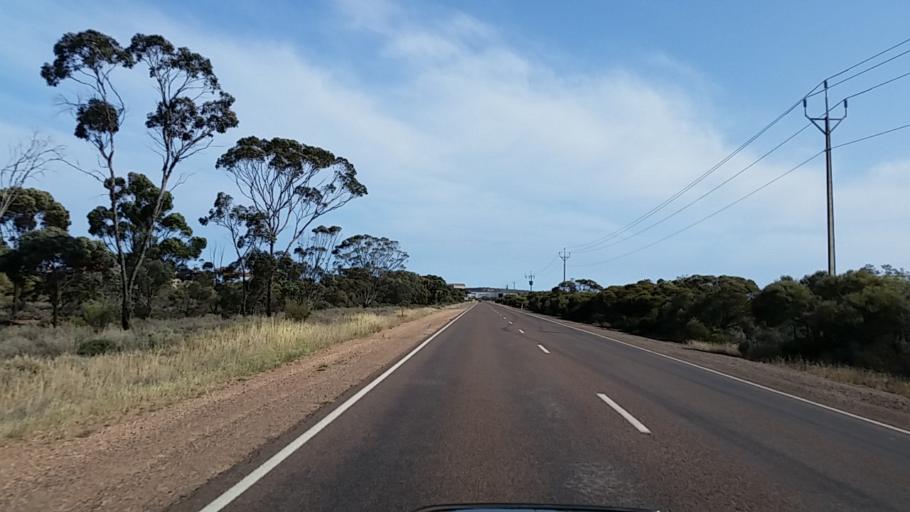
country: AU
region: South Australia
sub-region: Whyalla
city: Whyalla
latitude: -32.9931
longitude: 137.5792
